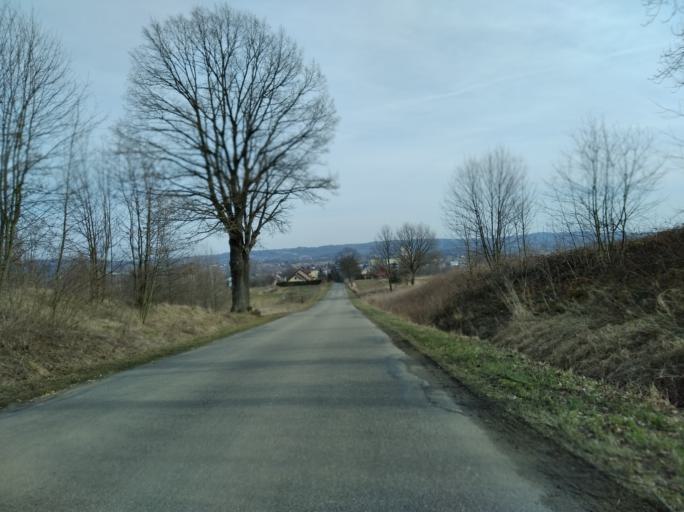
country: PL
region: Subcarpathian Voivodeship
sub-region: Powiat brzozowski
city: Stara Wies
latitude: 49.7138
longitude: 21.9980
